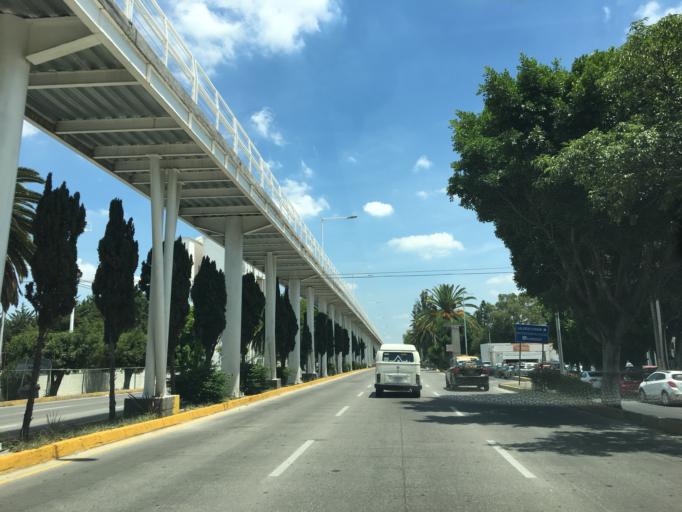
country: MX
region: Puebla
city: Puebla
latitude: 19.0665
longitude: -98.2237
